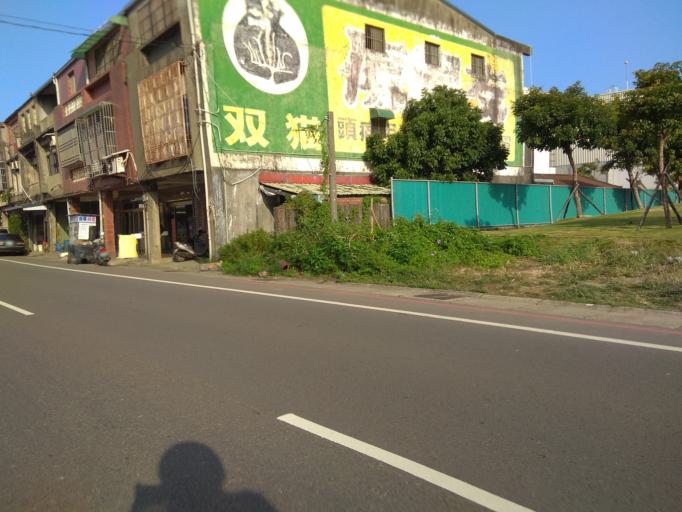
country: TW
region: Taiwan
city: Taoyuan City
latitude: 24.9632
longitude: 121.1550
